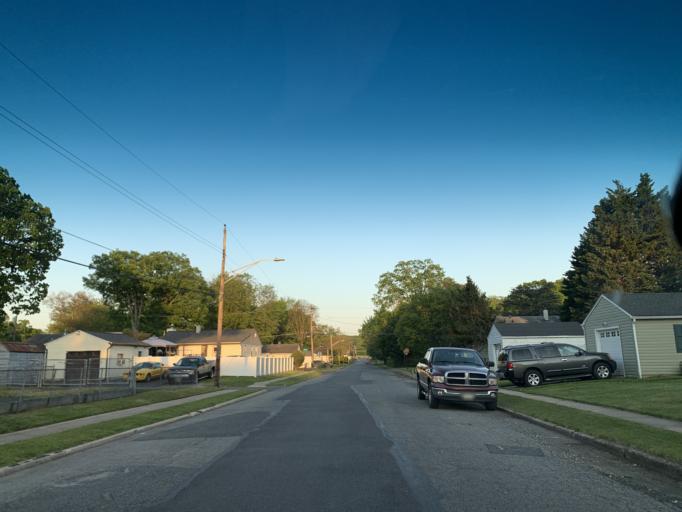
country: US
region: Maryland
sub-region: Harford County
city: Aberdeen
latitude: 39.5034
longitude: -76.1740
